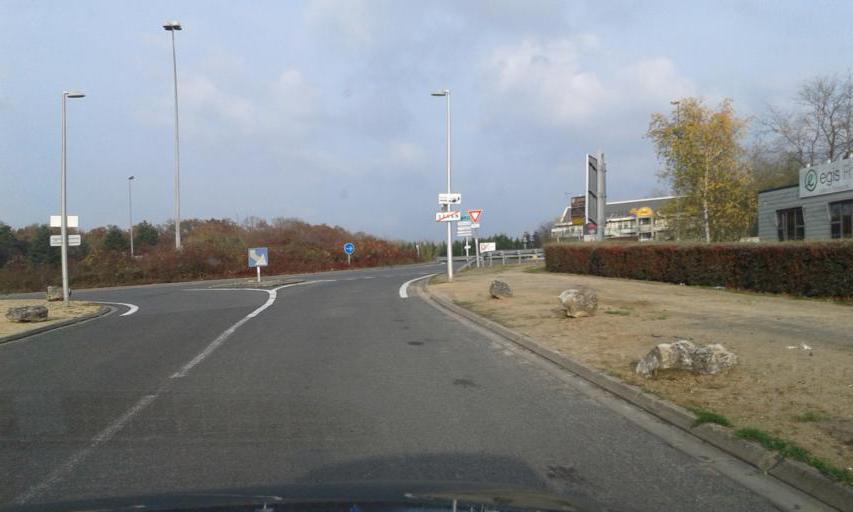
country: FR
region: Centre
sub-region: Departement du Loiret
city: Saran
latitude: 47.9468
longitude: 1.8652
